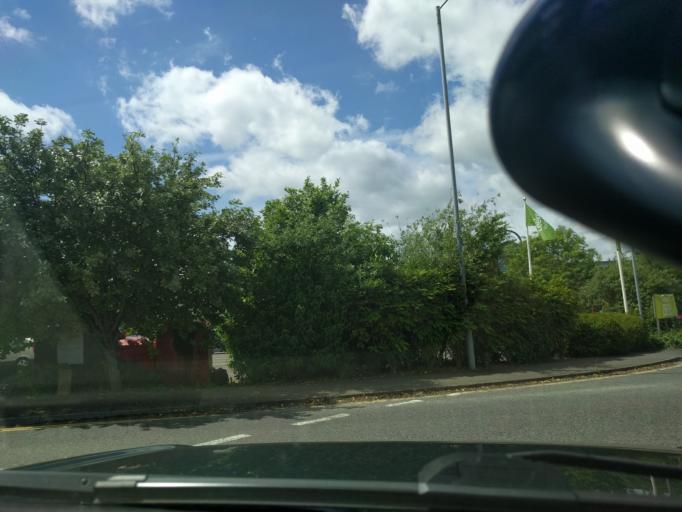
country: GB
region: England
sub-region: Wiltshire
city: Melksham
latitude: 51.3840
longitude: -2.1433
